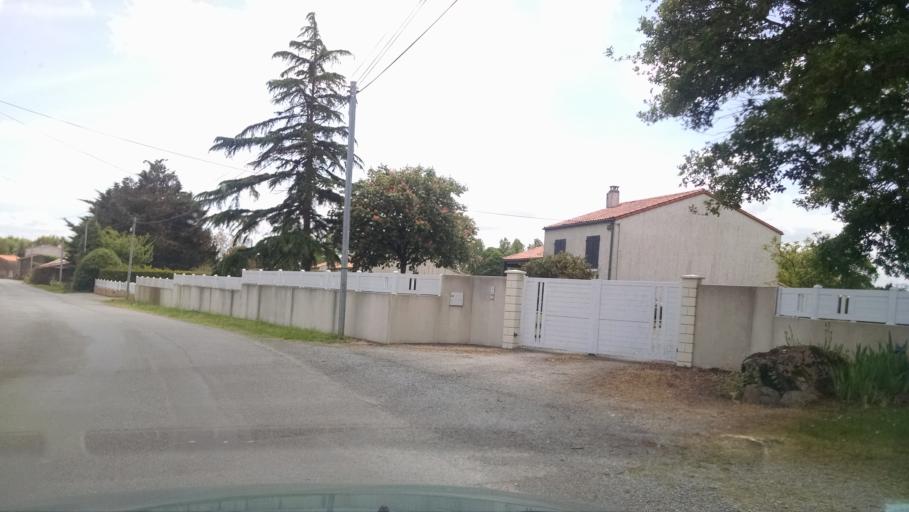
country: FR
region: Pays de la Loire
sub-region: Departement de la Loire-Atlantique
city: Gorges
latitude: 47.0881
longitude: -1.3077
